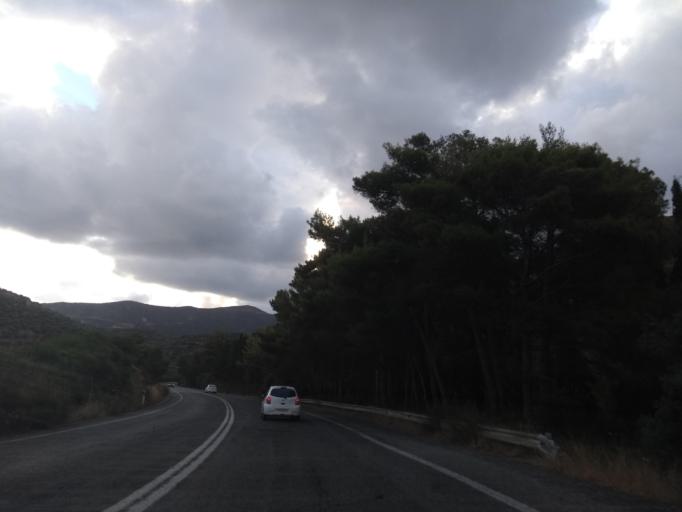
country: GR
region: Crete
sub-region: Nomos Rethymnis
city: Zoniana
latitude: 35.4014
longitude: 24.8600
